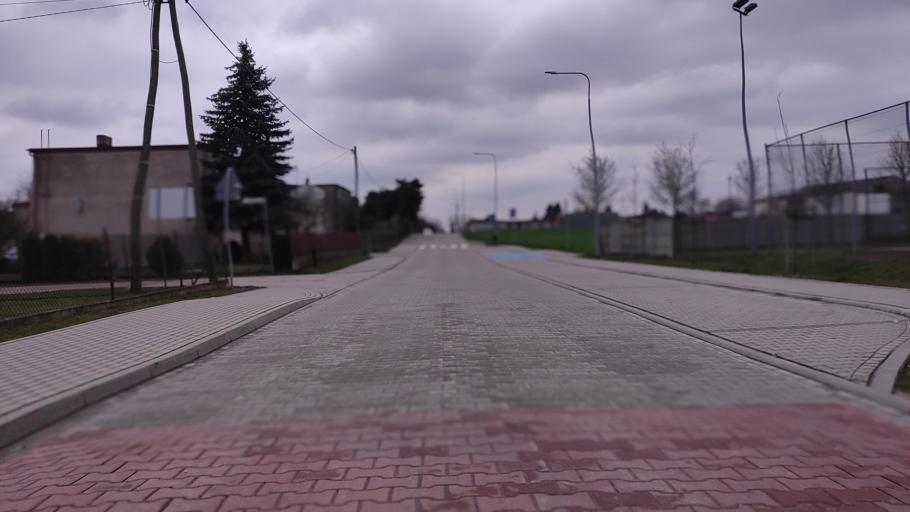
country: PL
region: Greater Poland Voivodeship
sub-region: Powiat poznanski
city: Kostrzyn
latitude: 52.4008
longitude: 17.1629
